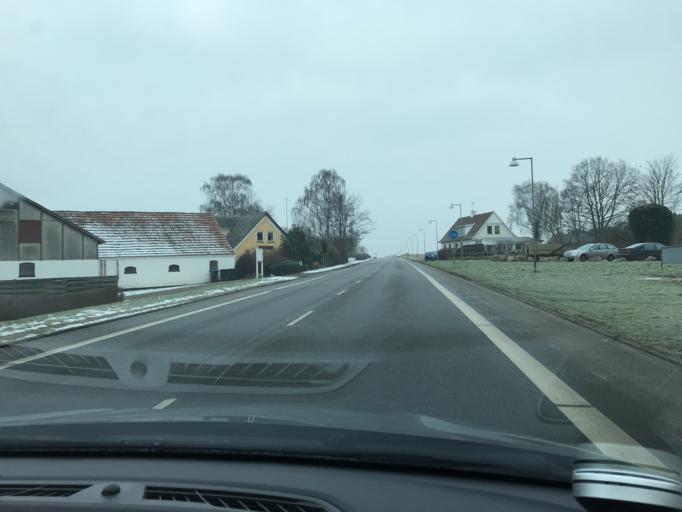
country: DK
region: Zealand
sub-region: Odsherred Kommune
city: Horve
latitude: 55.7569
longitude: 11.4518
